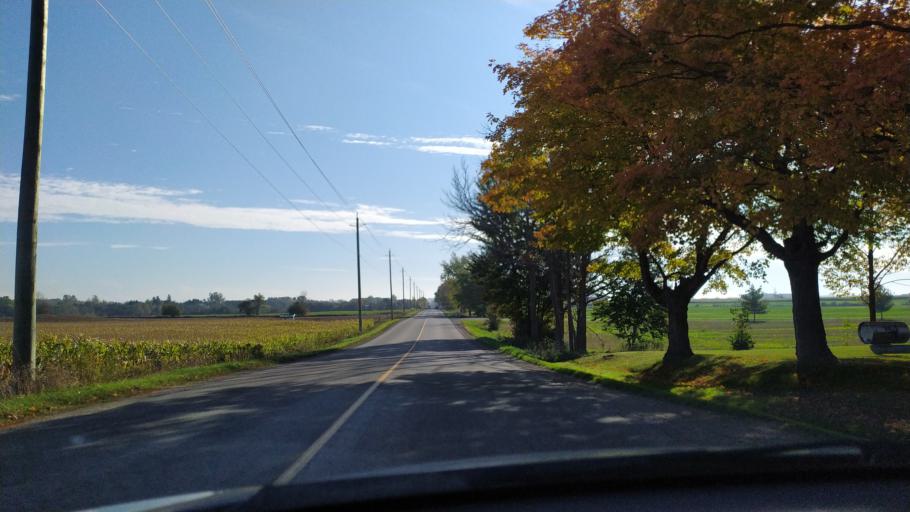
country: CA
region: Ontario
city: Waterloo
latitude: 43.4912
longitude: -80.7122
